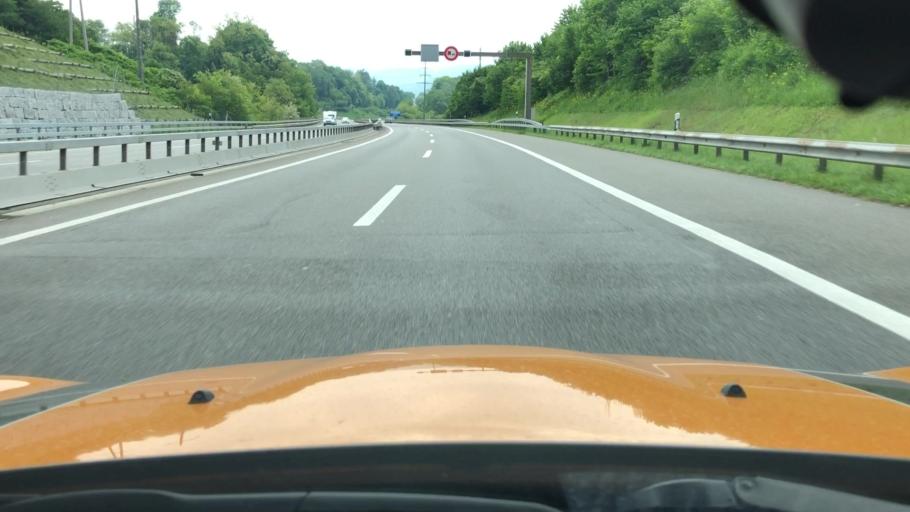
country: CH
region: Ticino
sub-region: Mendrisio District
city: Mendrisio
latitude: 45.8575
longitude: 8.9741
